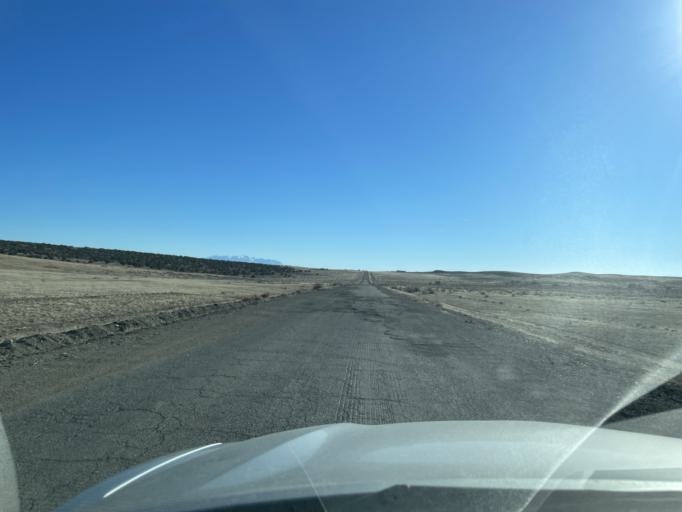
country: US
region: Colorado
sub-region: Mesa County
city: Loma
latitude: 39.1929
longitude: -109.1244
